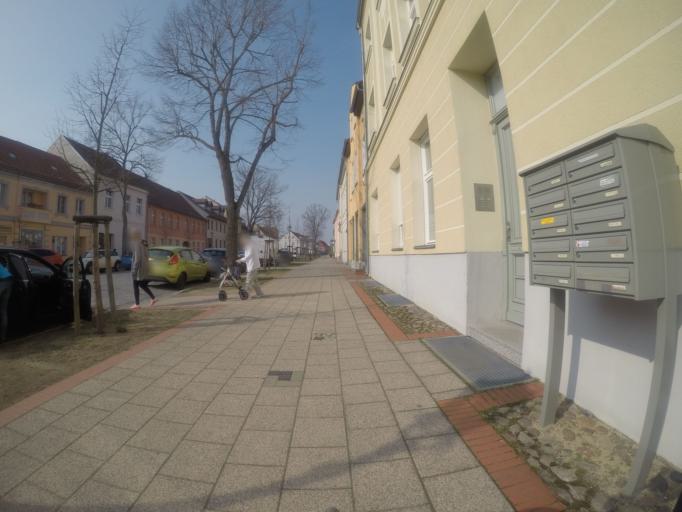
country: DE
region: Brandenburg
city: Mittenwalde
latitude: 52.2629
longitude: 13.5374
